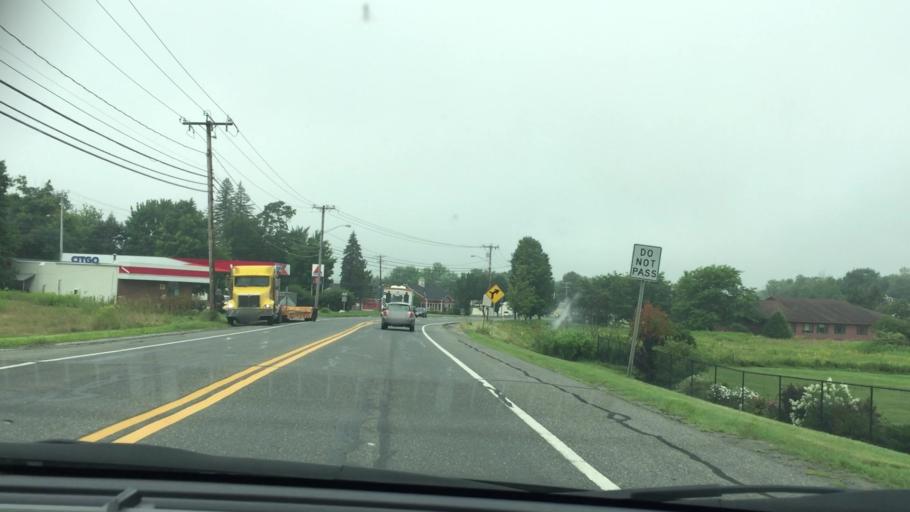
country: US
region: Massachusetts
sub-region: Berkshire County
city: Pittsfield
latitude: 42.4323
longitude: -73.3150
